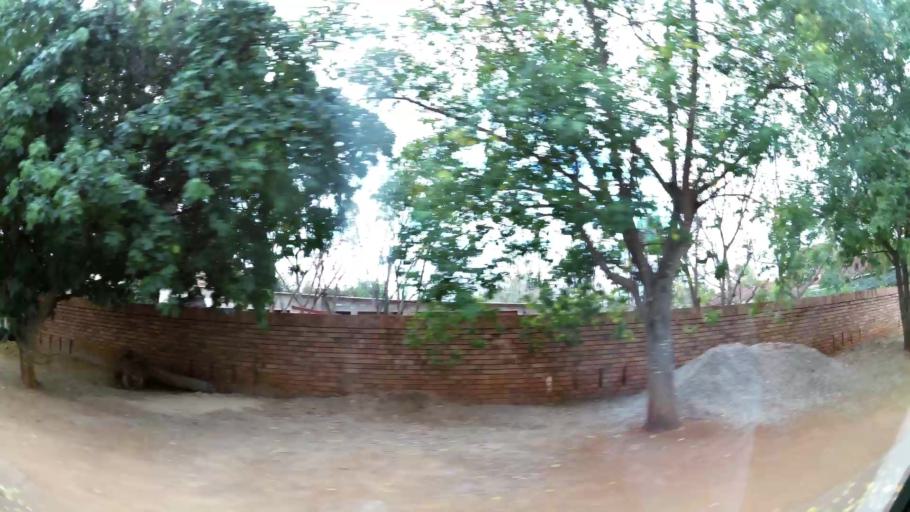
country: ZA
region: Limpopo
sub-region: Waterberg District Municipality
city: Modimolle
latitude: -24.5132
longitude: 28.7093
